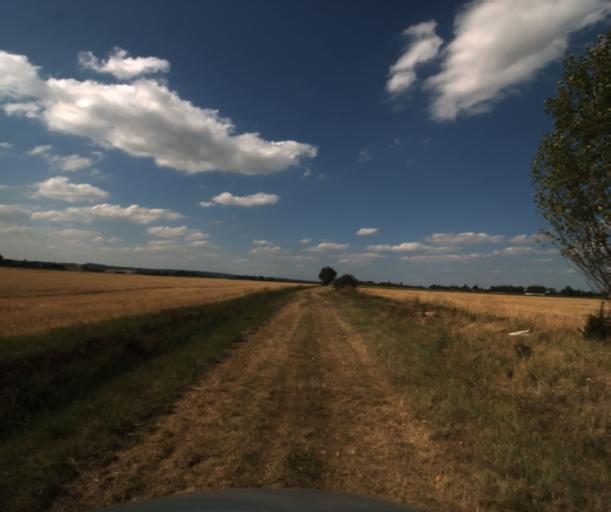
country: FR
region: Midi-Pyrenees
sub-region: Departement de la Haute-Garonne
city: Saint-Lys
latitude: 43.5210
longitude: 1.1773
